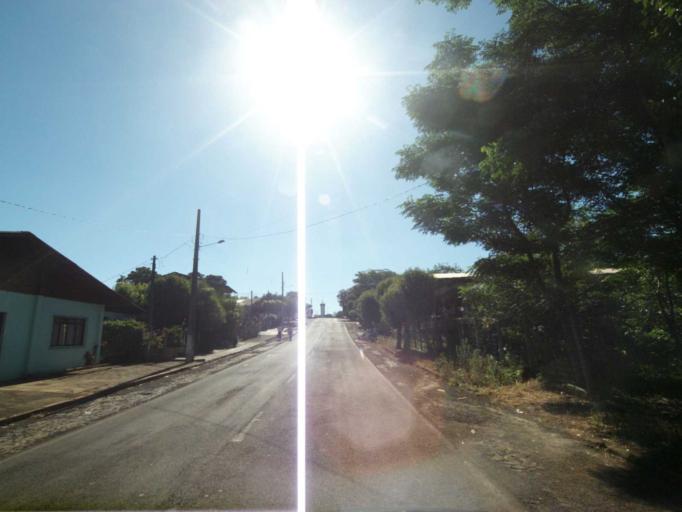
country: BR
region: Parana
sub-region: Coronel Vivida
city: Coronel Vivida
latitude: -25.9646
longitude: -52.8119
